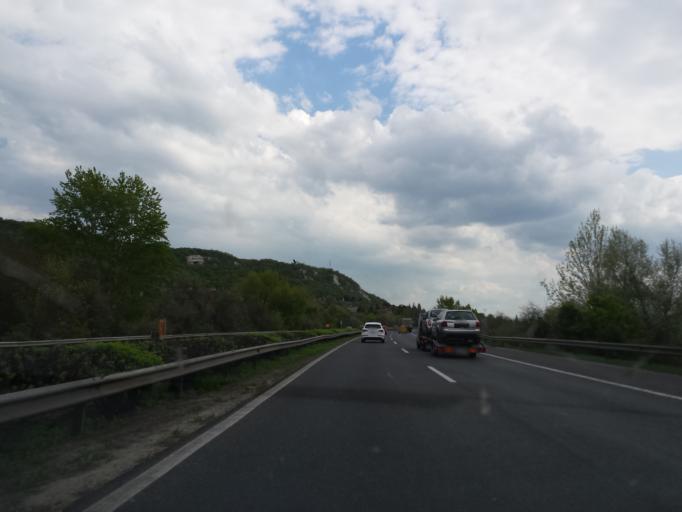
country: HU
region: Komarom-Esztergom
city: Tatabanya
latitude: 47.5945
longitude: 18.3961
